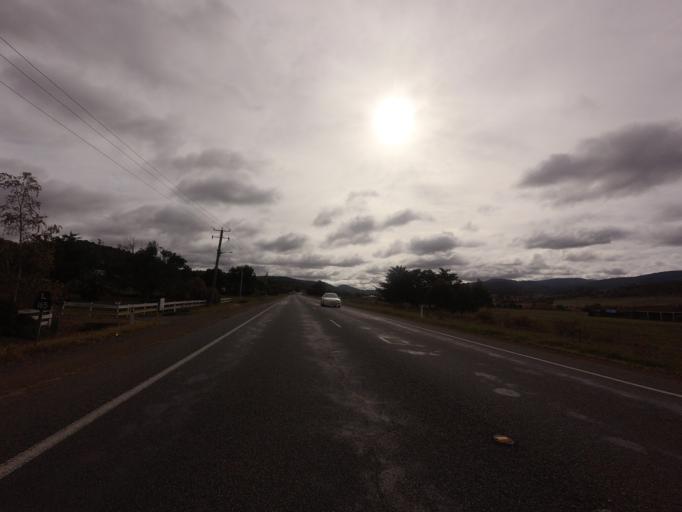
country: AU
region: Tasmania
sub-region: Brighton
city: Bridgewater
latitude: -42.6393
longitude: 147.2283
